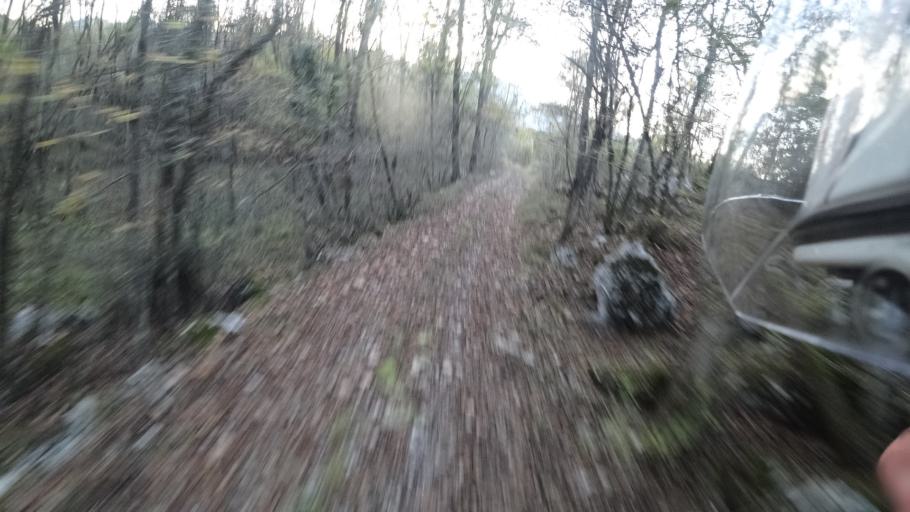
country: HR
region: Primorsko-Goranska
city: Matulji
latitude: 45.4072
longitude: 14.3130
